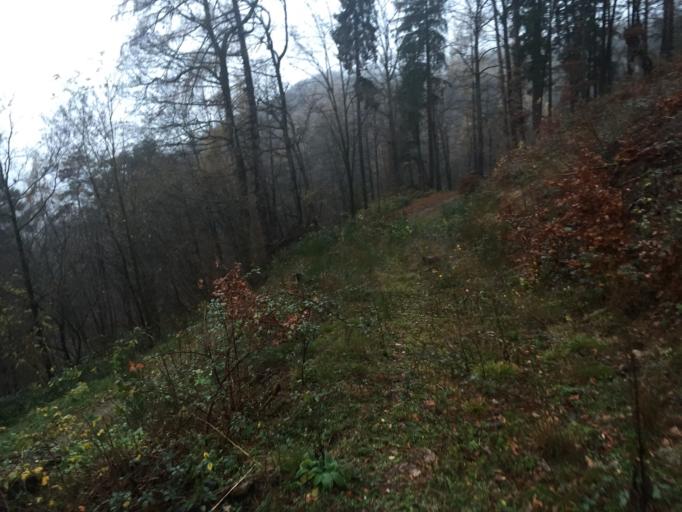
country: DE
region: Baden-Wuerttemberg
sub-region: Karlsruhe Region
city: Eberbach
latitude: 49.4646
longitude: 9.0063
